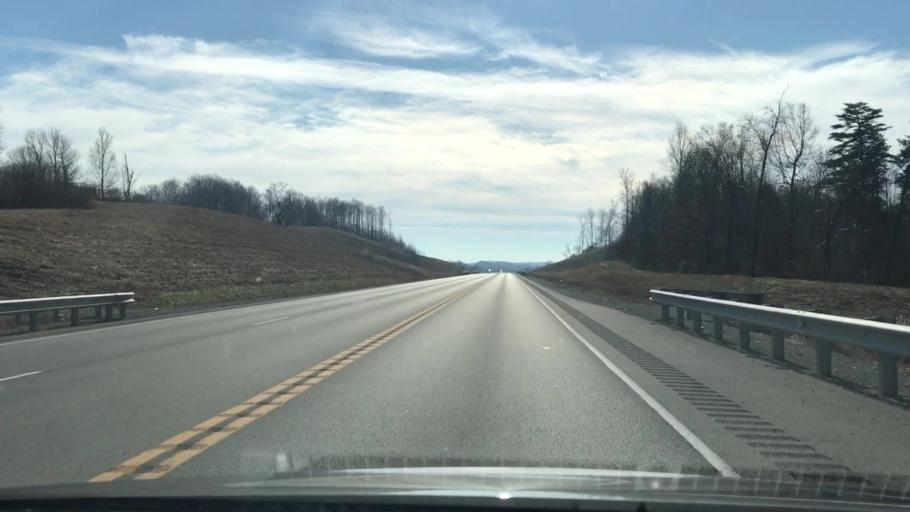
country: US
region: Kentucky
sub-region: Metcalfe County
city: Edmonton
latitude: 36.8524
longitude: -85.6745
